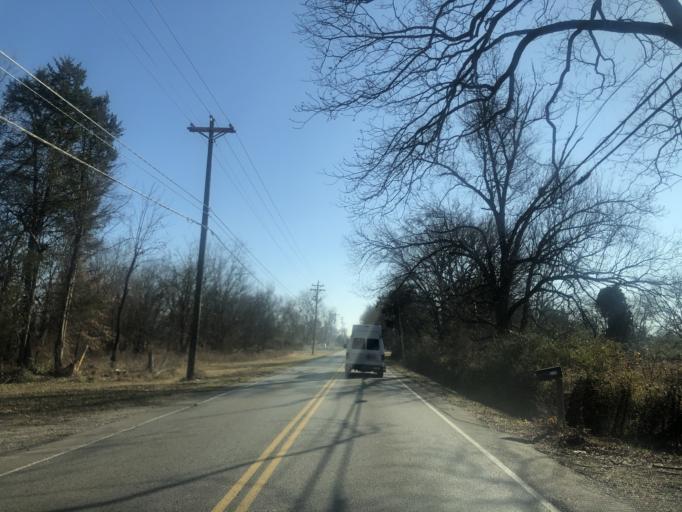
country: US
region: Tennessee
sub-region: Rutherford County
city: Smyrna
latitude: 35.9197
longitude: -86.4768
